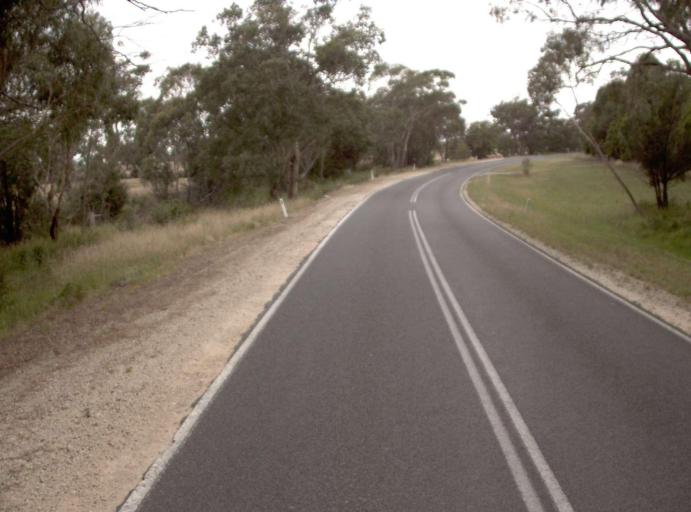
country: AU
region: Victoria
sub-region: Wellington
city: Sale
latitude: -38.1769
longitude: 147.1501
